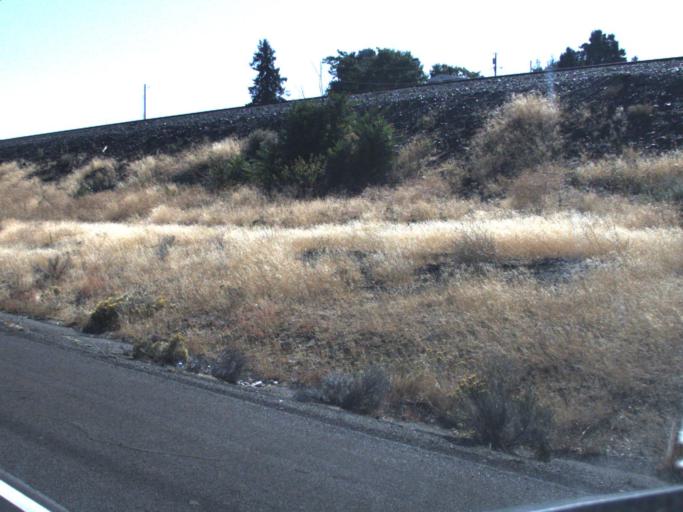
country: US
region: Washington
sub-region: Franklin County
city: West Pasco
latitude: 46.2236
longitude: -119.1669
